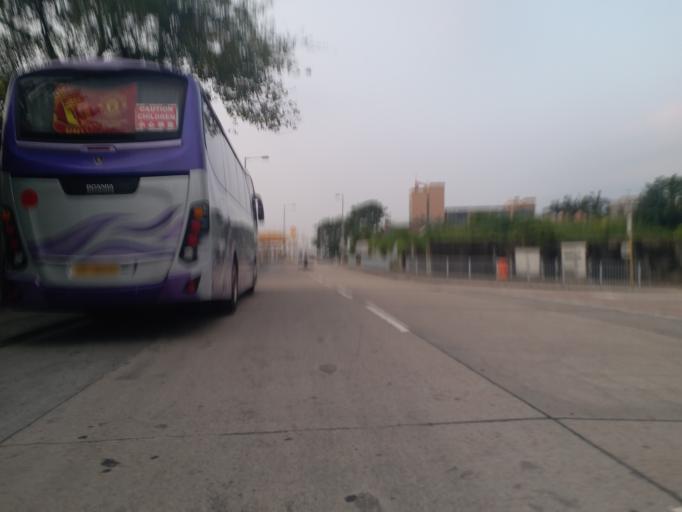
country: HK
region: Yuen Long
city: Yuen Long Kau Hui
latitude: 22.4385
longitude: 114.0112
